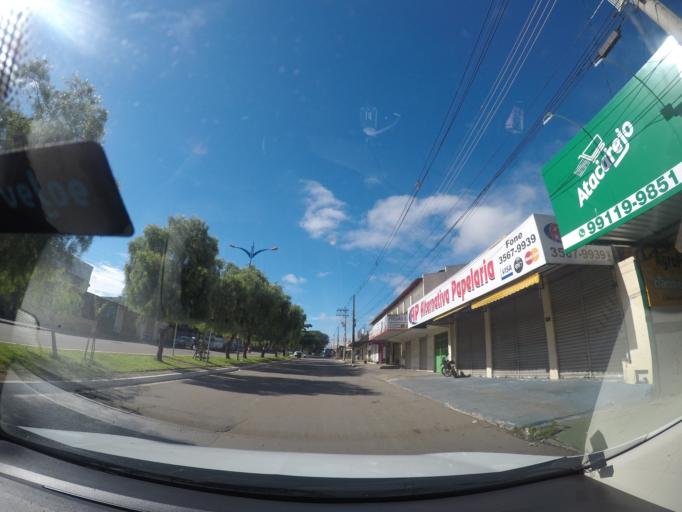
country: BR
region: Goias
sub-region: Senador Canedo
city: Senador Canedo
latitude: -16.6502
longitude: -49.1570
